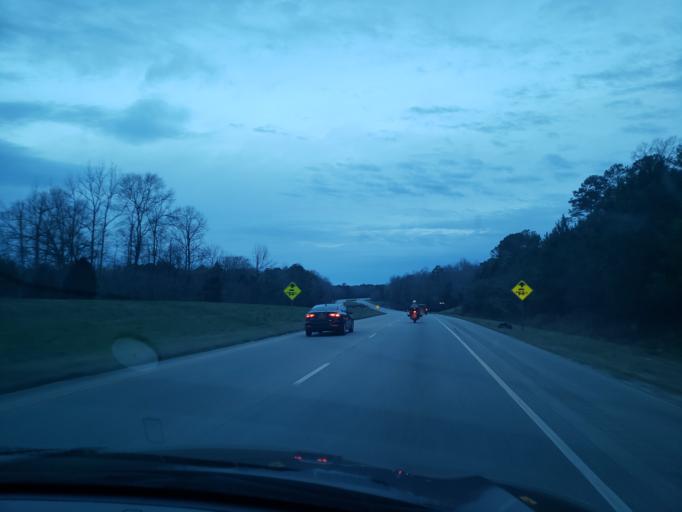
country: US
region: Alabama
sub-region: Lee County
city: Auburn
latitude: 32.6566
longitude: -85.4550
